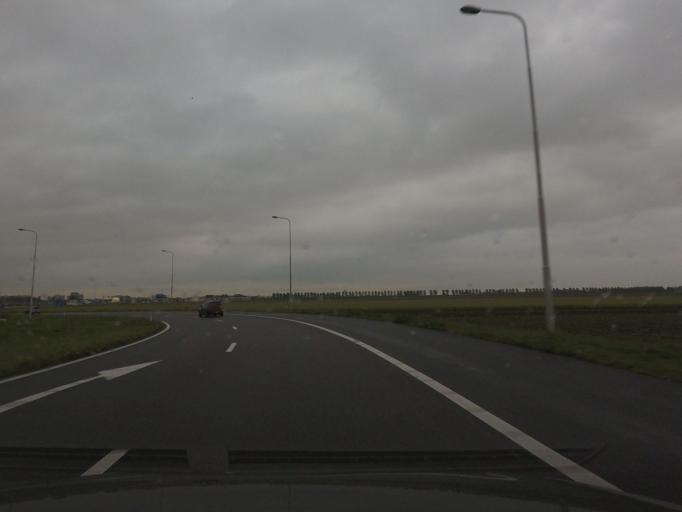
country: NL
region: North Holland
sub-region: Gemeente Haarlemmermeer
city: Hoofddorp
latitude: 52.2718
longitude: 4.7079
